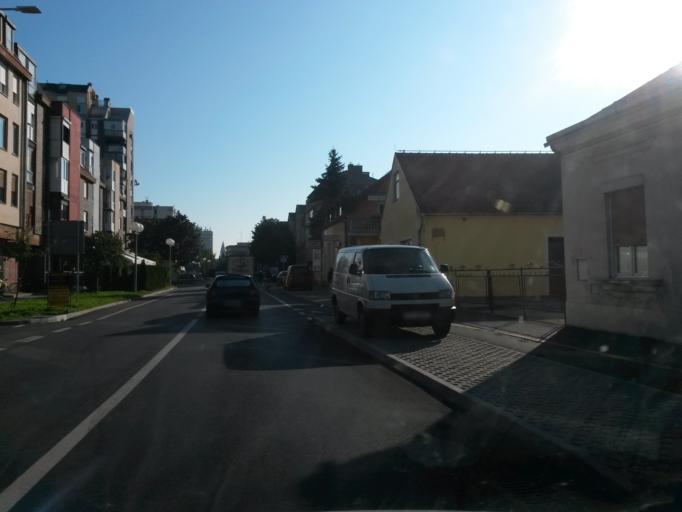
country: HR
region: Varazdinska
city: Varazdin
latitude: 46.3048
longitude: 16.3274
